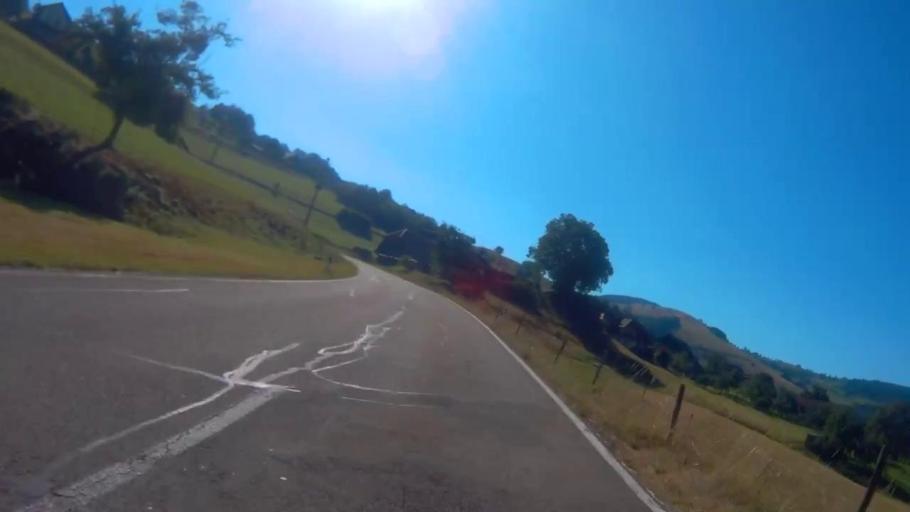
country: DE
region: Baden-Wuerttemberg
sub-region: Freiburg Region
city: Wembach
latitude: 47.7648
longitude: 7.8899
